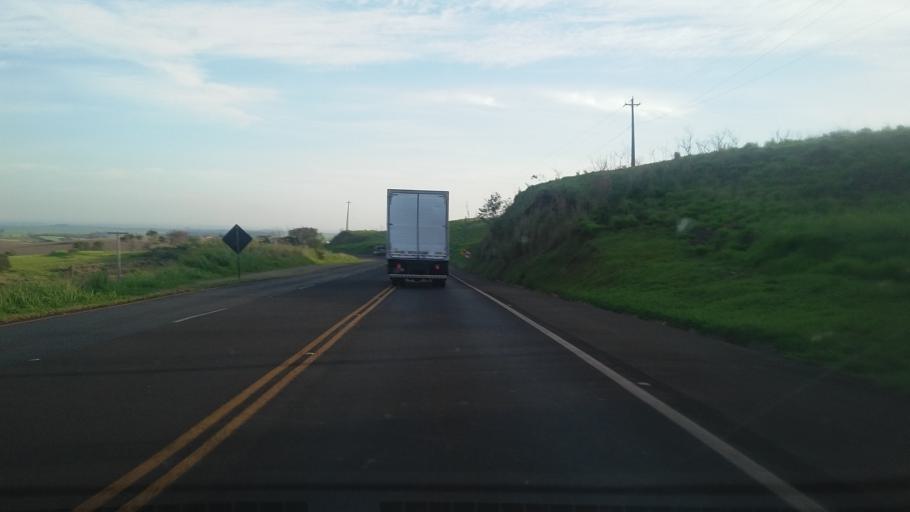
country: BR
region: Parana
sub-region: Bandeirantes
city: Bandeirantes
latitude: -23.1732
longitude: -50.6142
